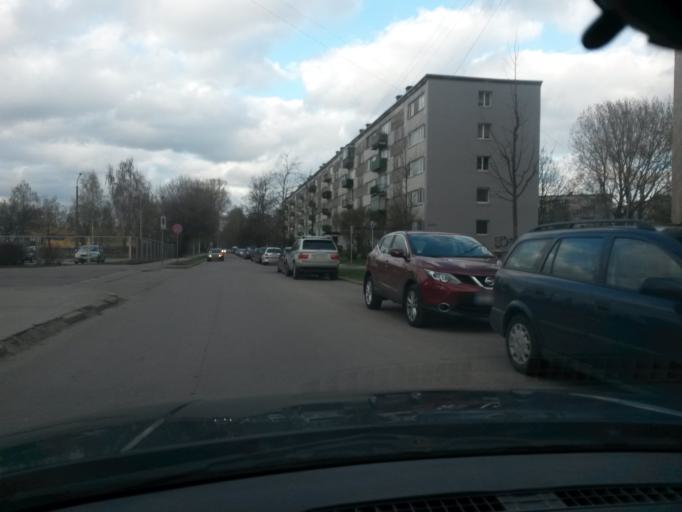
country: LV
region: Kekava
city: Balozi
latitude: 56.9151
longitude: 24.1667
